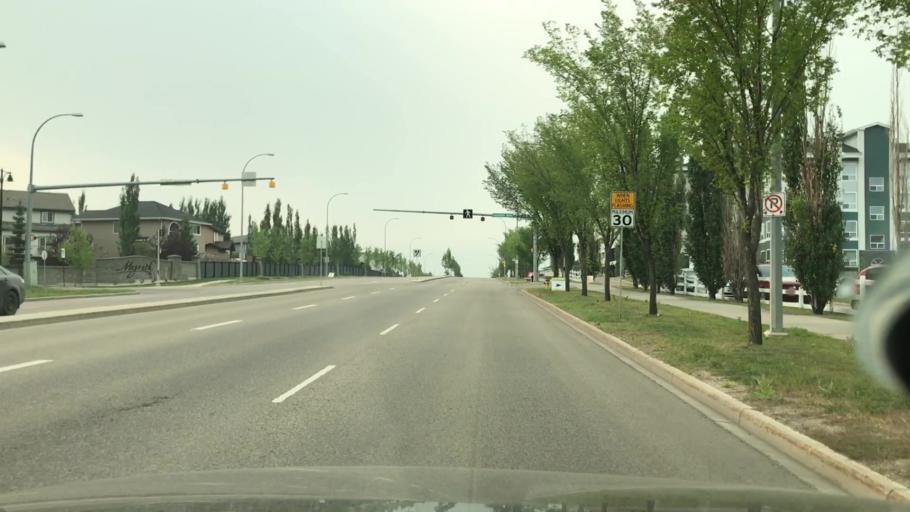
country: CA
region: Alberta
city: Edmonton
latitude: 53.4498
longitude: -113.5656
